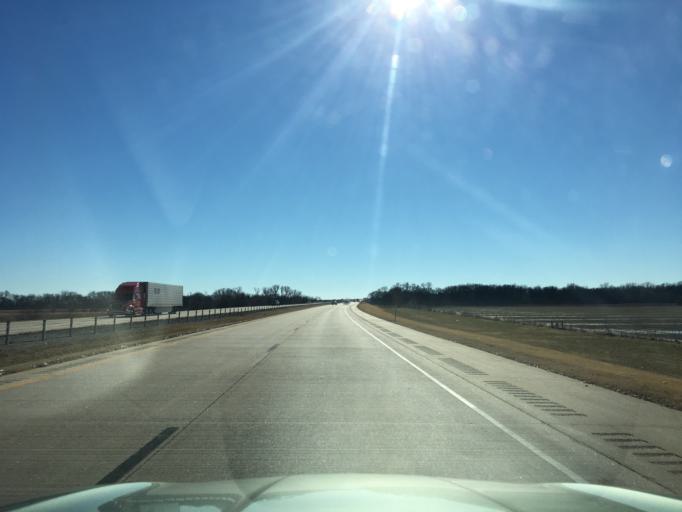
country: US
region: Oklahoma
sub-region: Noble County
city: Perry
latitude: 36.4821
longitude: -97.3273
